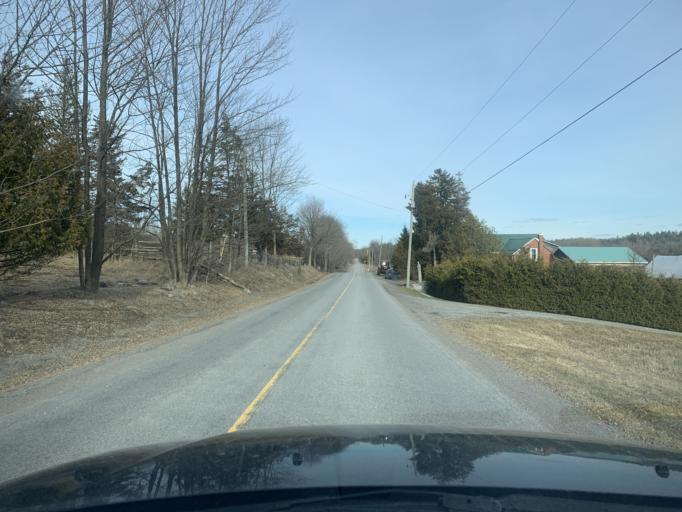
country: CA
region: Ontario
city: Greater Napanee
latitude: 44.4393
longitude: -77.0847
